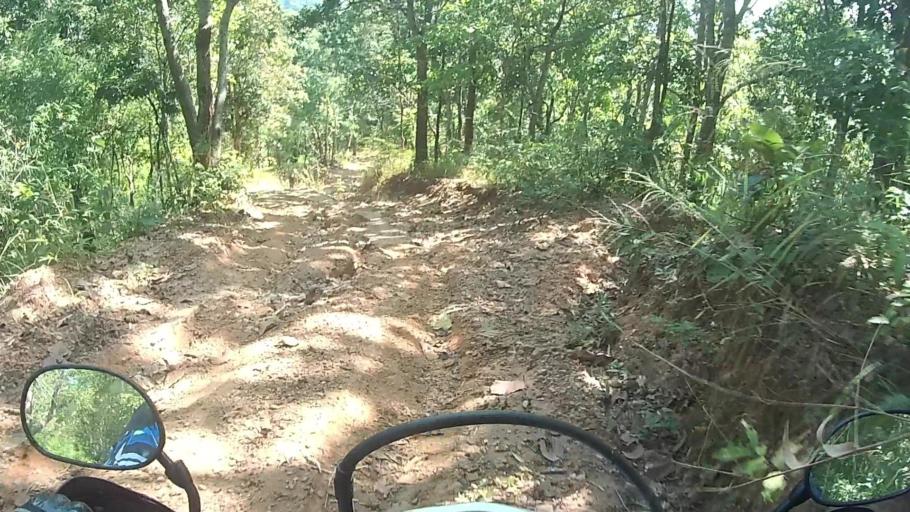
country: TH
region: Chiang Mai
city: Mae On
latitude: 19.0292
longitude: 99.2951
